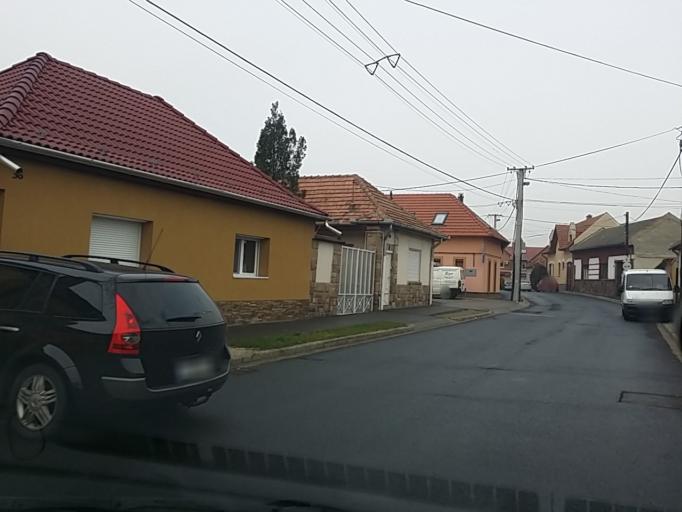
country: HU
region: Heves
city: Gyongyos
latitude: 47.7891
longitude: 19.9296
